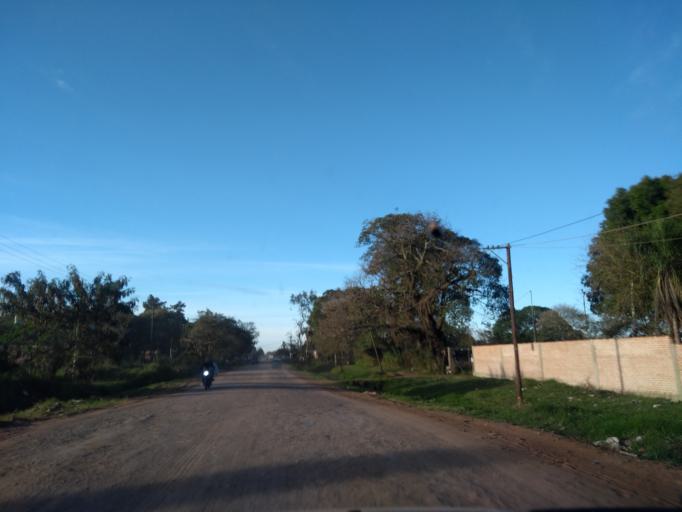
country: AR
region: Chaco
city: Resistencia
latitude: -27.4904
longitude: -58.9731
